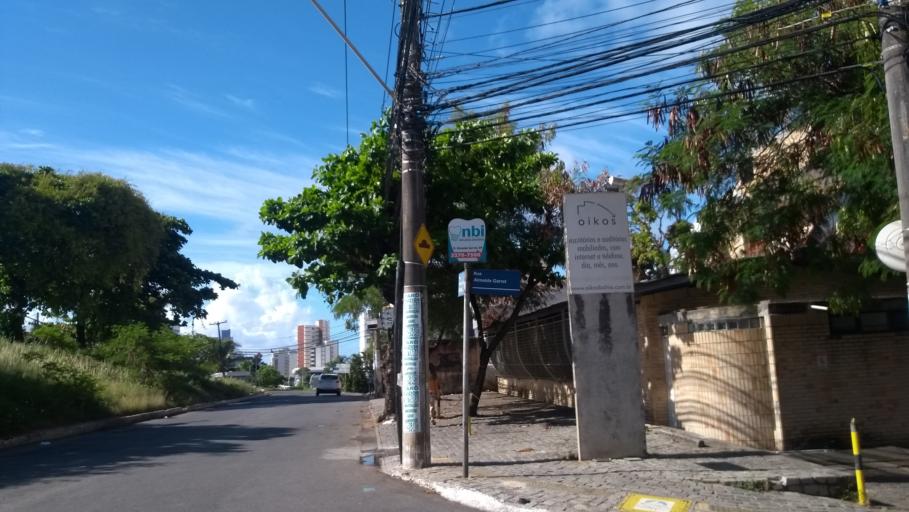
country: BR
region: Bahia
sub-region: Salvador
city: Salvador
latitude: -12.9985
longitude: -38.4596
